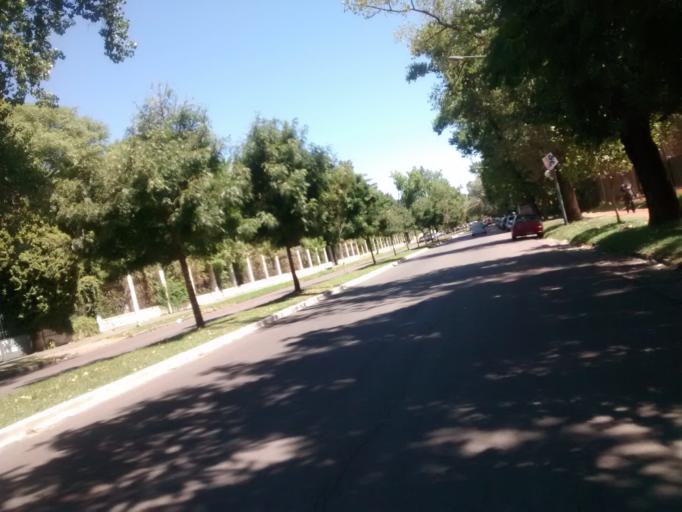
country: AR
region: Buenos Aires
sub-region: Partido de La Plata
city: La Plata
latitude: -34.9053
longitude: -57.9370
